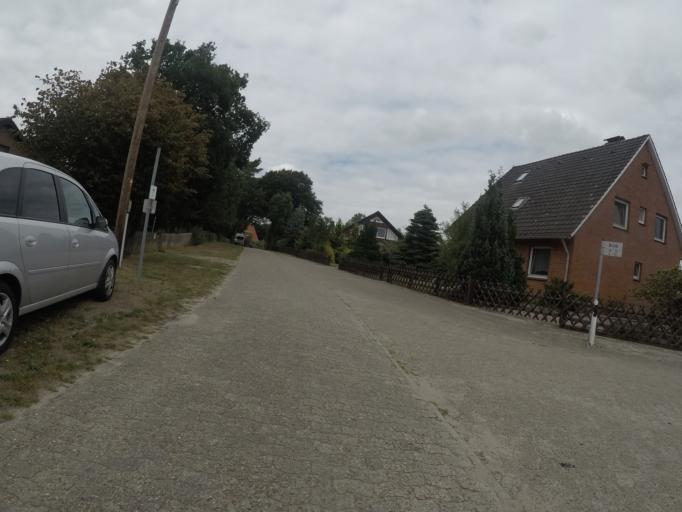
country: DE
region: Lower Saxony
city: Wingst
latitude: 53.7111
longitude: 9.0675
